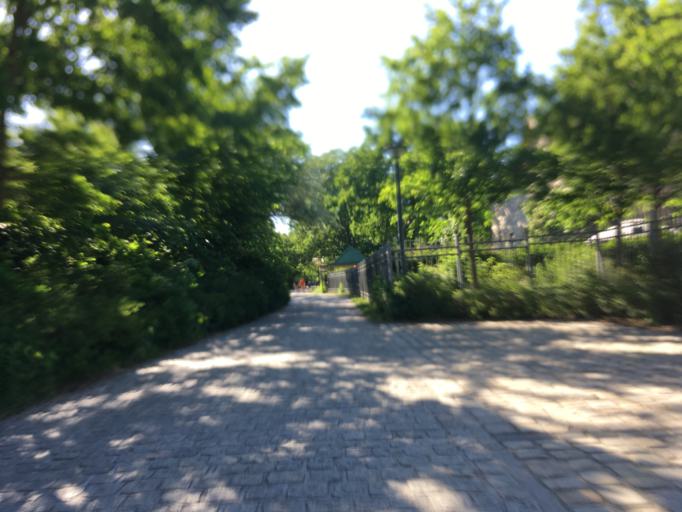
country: DE
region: Berlin
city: Oberschoneweide
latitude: 52.4685
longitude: 13.5351
